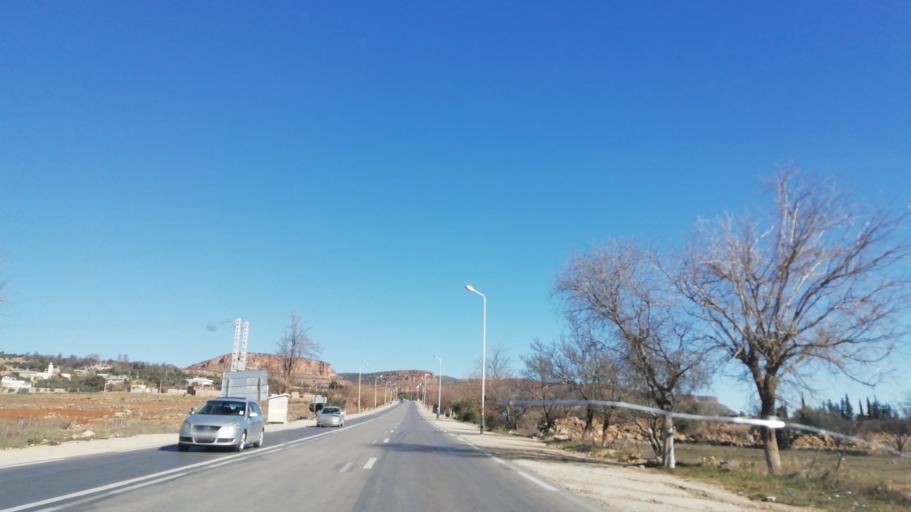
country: DZ
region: Tlemcen
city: Sebdou
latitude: 34.6736
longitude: -1.3172
